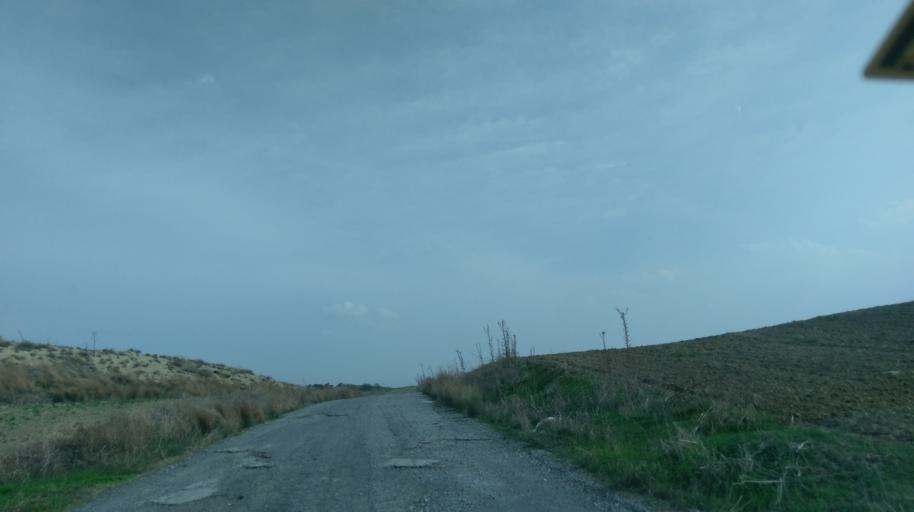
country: CY
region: Keryneia
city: Lapithos
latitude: 35.2647
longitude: 33.1179
